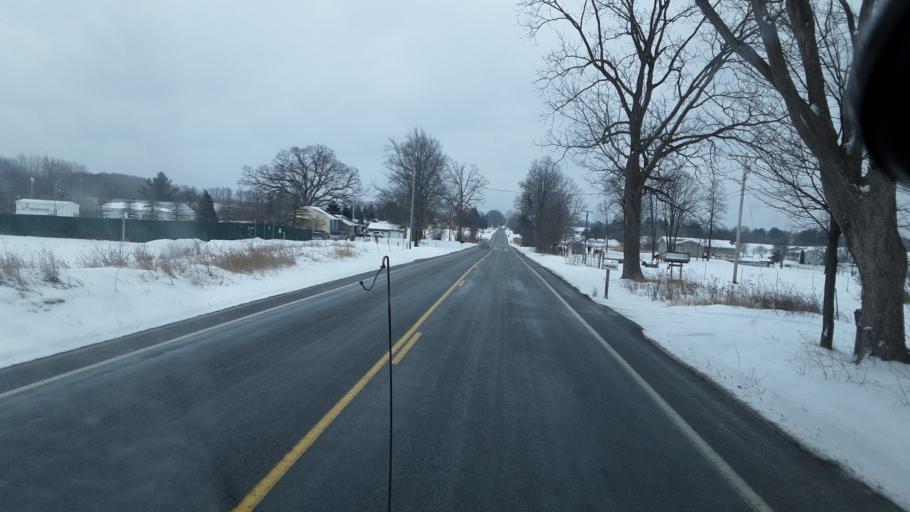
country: US
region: Michigan
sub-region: Ingham County
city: Leslie
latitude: 42.4308
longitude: -84.4136
